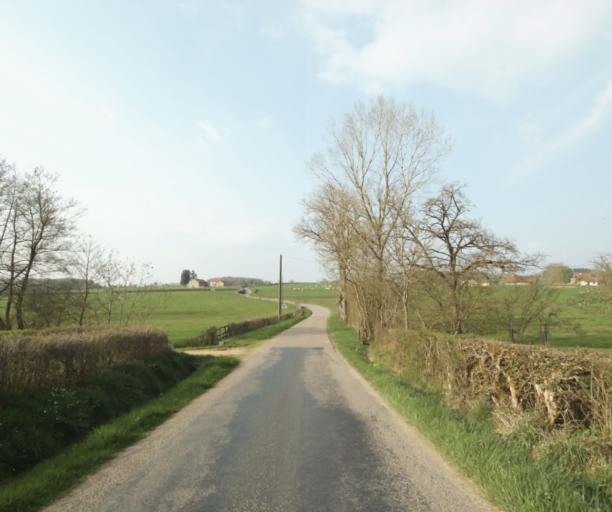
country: FR
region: Bourgogne
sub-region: Departement de Saone-et-Loire
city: Matour
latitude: 46.4681
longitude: 4.4527
